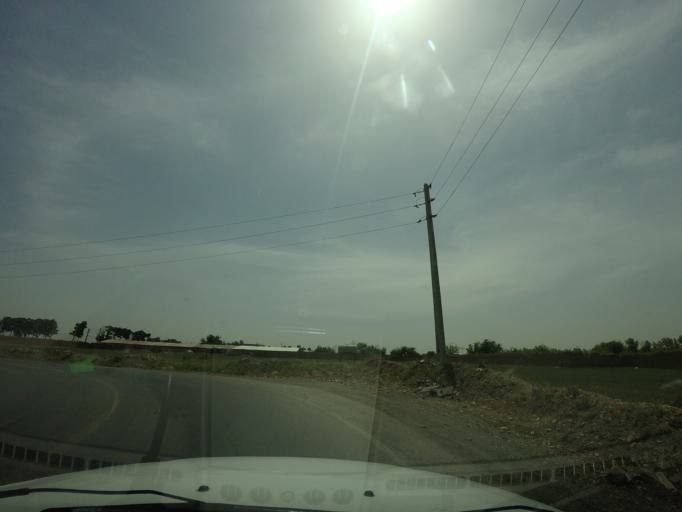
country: IR
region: Tehran
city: Eslamshahr
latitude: 35.5961
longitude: 51.2568
